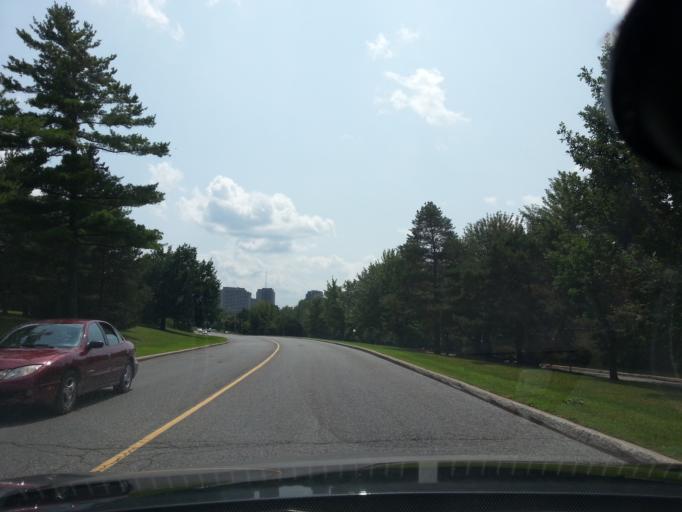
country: CA
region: Ontario
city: Ottawa
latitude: 45.3808
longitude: -75.7014
